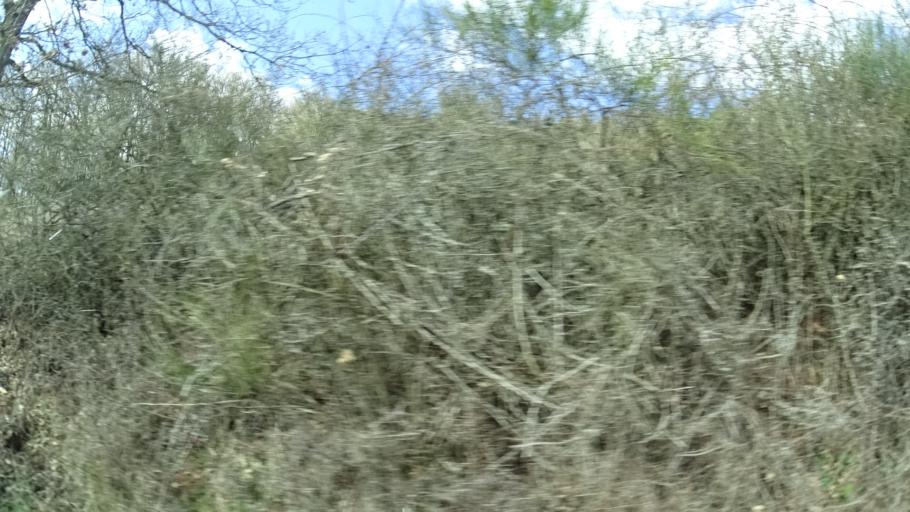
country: DE
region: Rheinland-Pfalz
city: Fischbach
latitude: 49.7452
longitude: 7.3971
